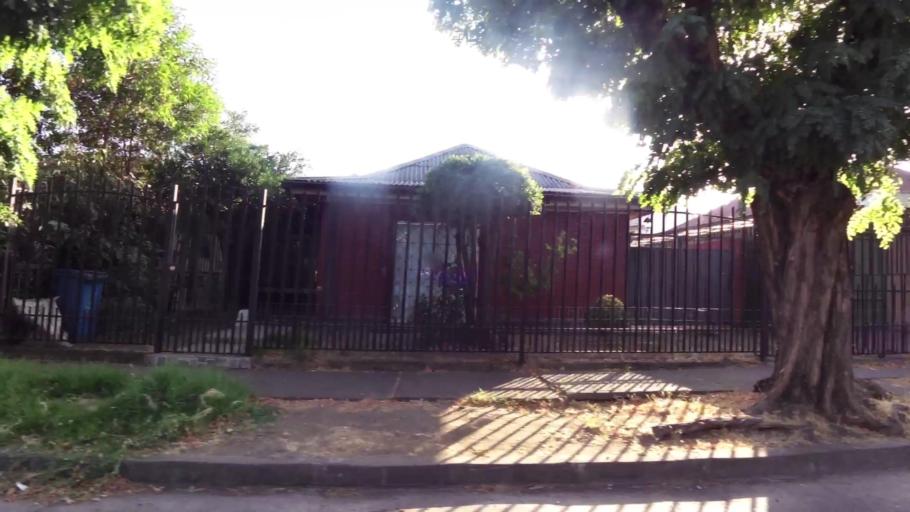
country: CL
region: Maule
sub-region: Provincia de Talca
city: Talca
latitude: -35.4135
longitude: -71.6566
